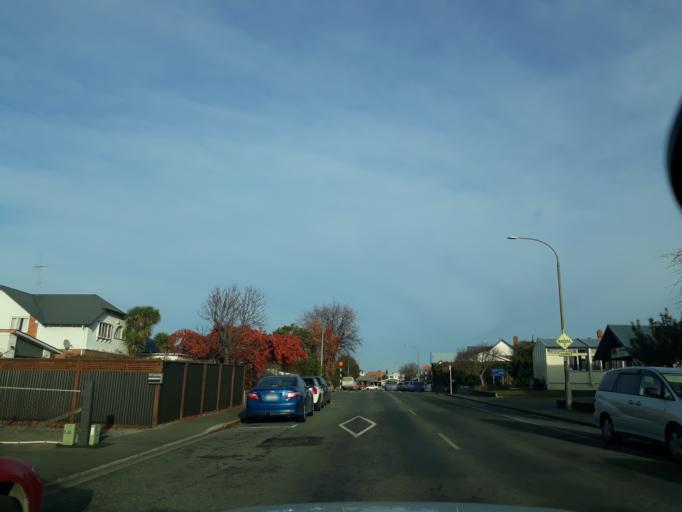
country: NZ
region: Canterbury
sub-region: Timaru District
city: Timaru
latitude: -44.3883
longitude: 171.2388
